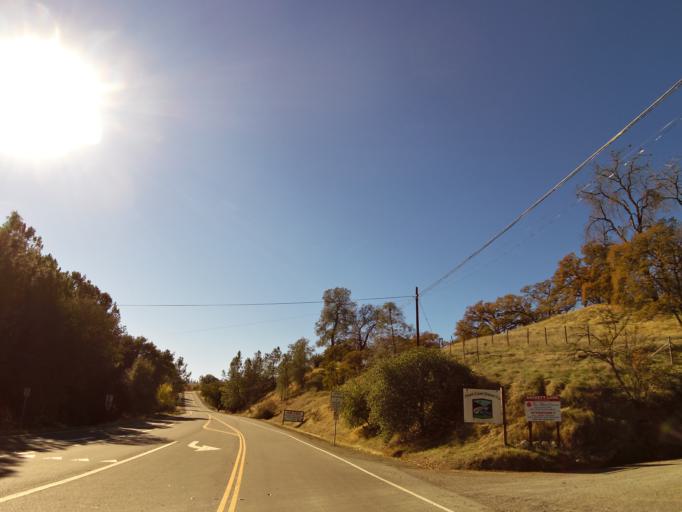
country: US
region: California
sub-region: Yolo County
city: Winters
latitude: 38.4924
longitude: -122.0293
